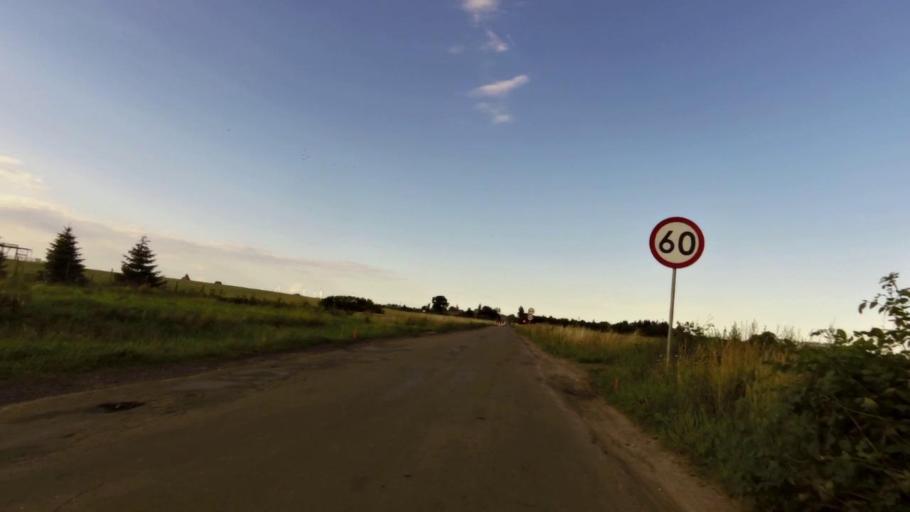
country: PL
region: West Pomeranian Voivodeship
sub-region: Powiat slawienski
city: Darlowo
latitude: 54.4068
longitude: 16.3885
